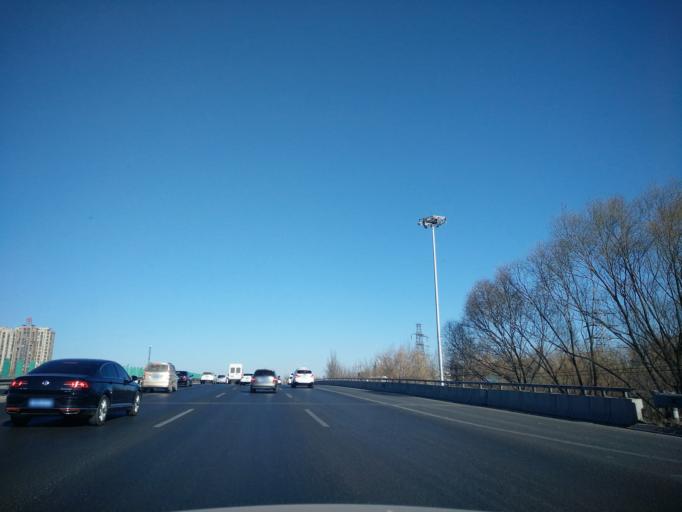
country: CN
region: Beijing
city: Huaxiang
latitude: 39.8303
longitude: 116.3398
